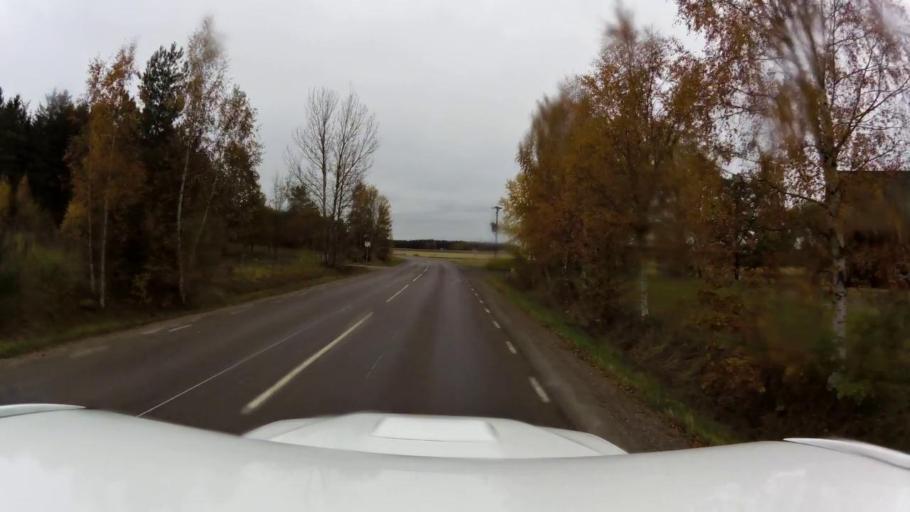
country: SE
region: OEstergoetland
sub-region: Linkopings Kommun
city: Linghem
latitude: 58.4392
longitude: 15.7147
